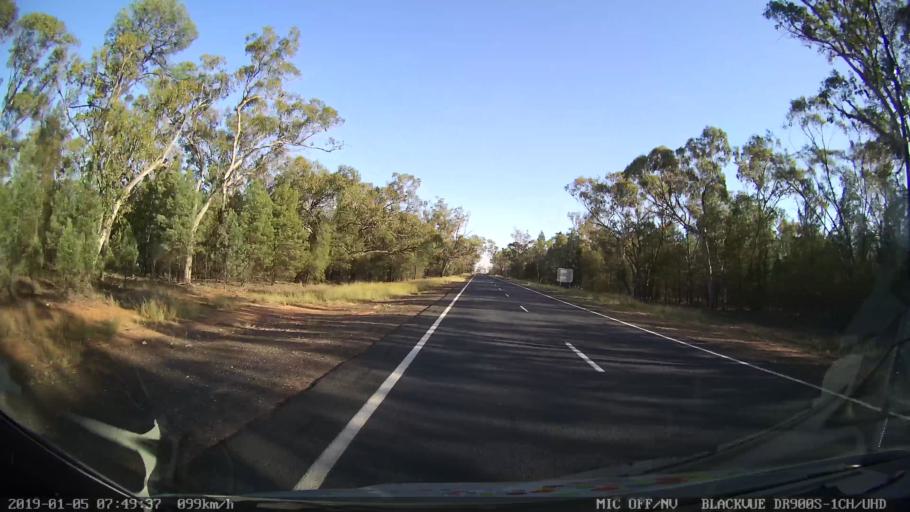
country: AU
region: New South Wales
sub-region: Gilgandra
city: Gilgandra
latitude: -31.7991
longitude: 148.6361
